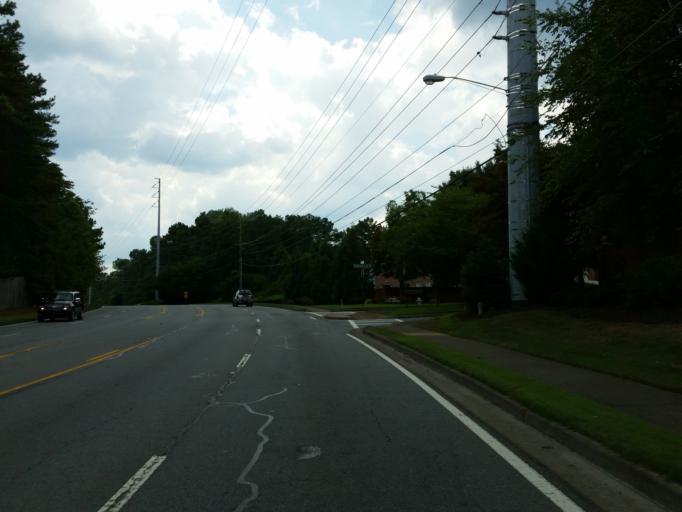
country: US
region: Georgia
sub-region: Fulton County
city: Roswell
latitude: 34.0373
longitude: -84.4481
